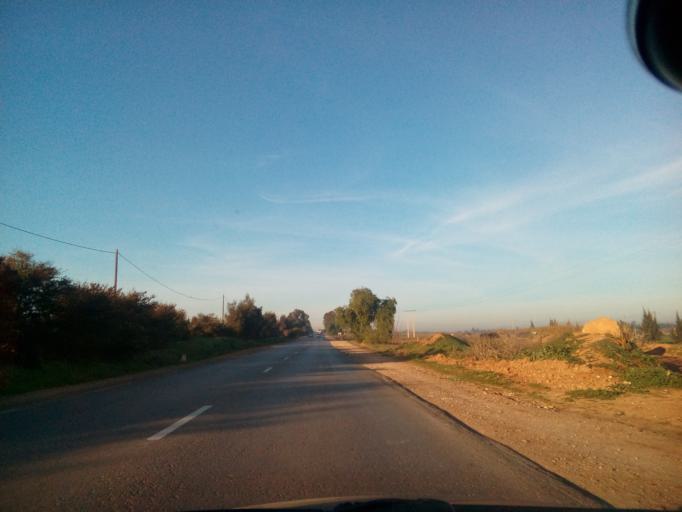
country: DZ
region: Relizane
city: Relizane
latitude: 35.7288
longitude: 0.4123
